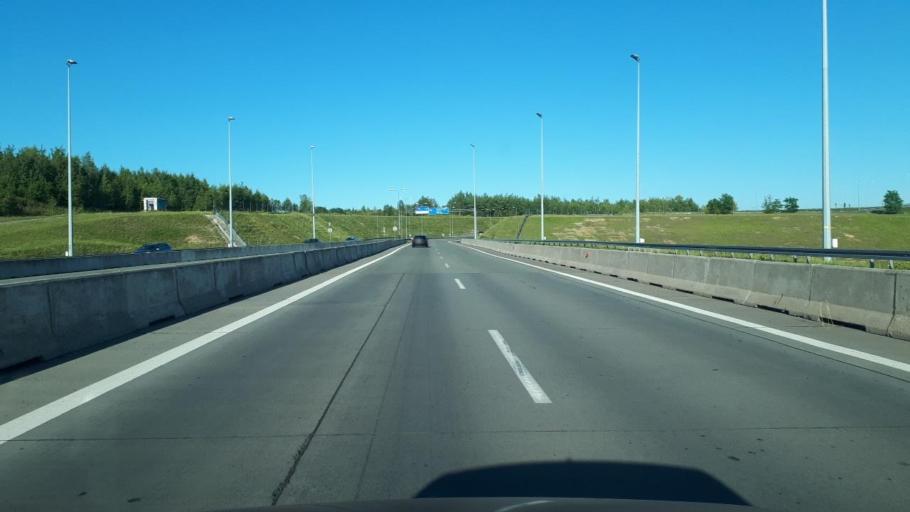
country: PL
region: Silesian Voivodeship
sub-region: Powiat tarnogorski
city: Radzionkow
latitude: 50.3745
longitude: 18.8954
